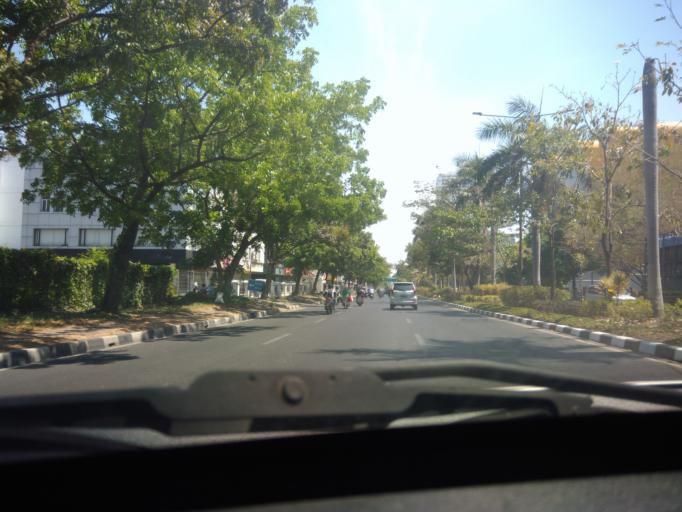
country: ID
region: East Java
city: Mulyorejo
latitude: -7.2853
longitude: 112.7809
